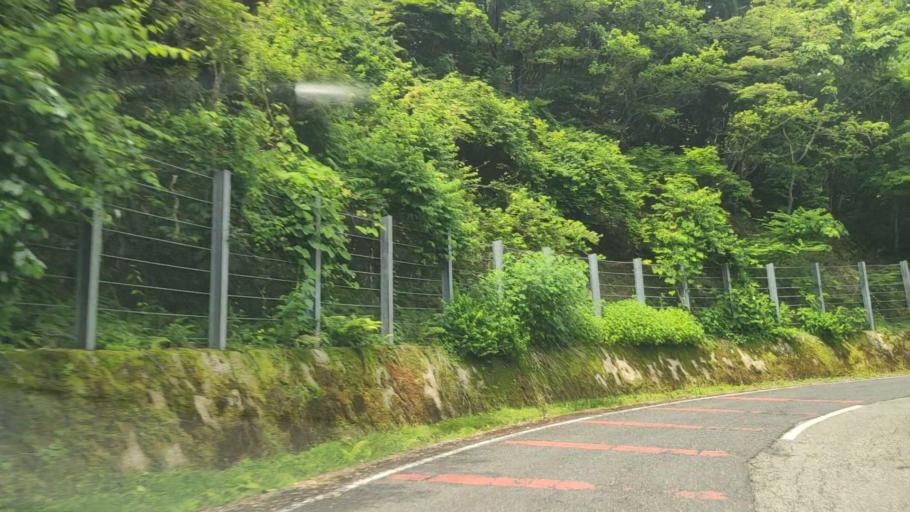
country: JP
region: Hyogo
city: Toyooka
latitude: 35.5167
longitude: 134.6868
